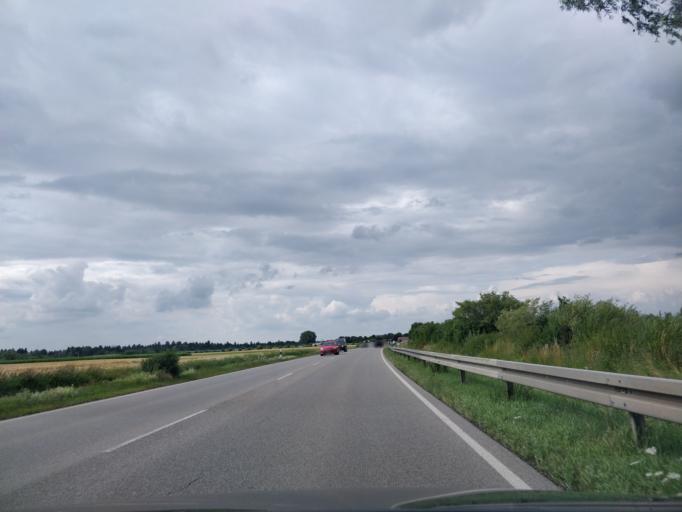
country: DE
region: Bavaria
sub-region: Swabia
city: Kissing
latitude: 48.2859
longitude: 10.9685
